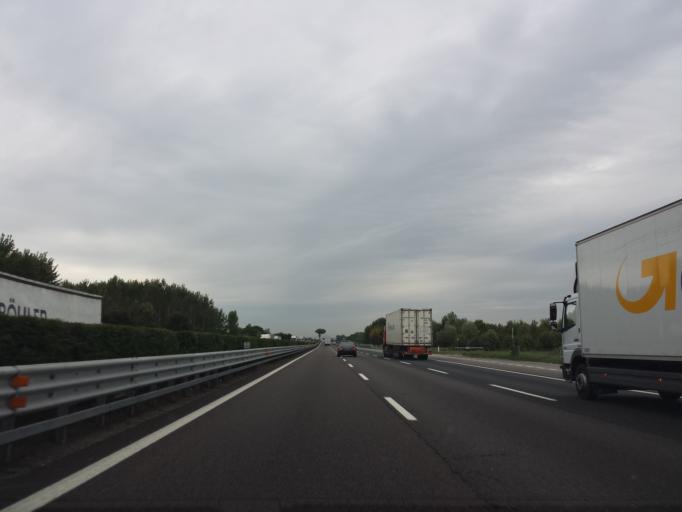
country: IT
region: Veneto
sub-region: Provincia di Padova
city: Oltre Brenta
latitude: 45.4299
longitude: 11.9945
